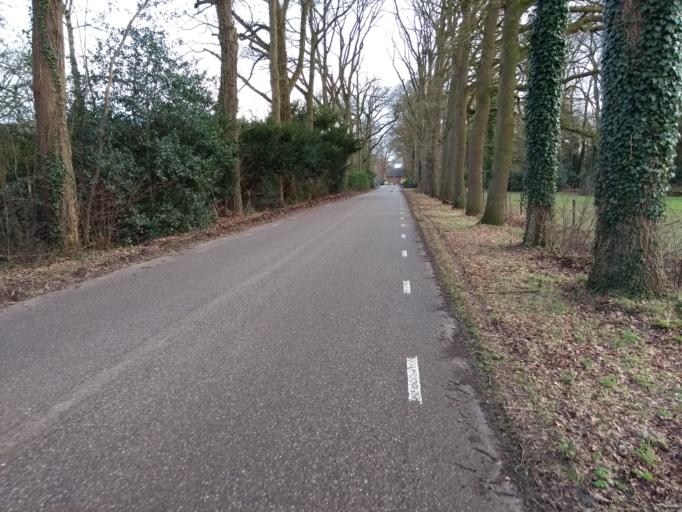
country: NL
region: Overijssel
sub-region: Gemeente Enschede
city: Enschede
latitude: 52.2518
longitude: 6.8851
